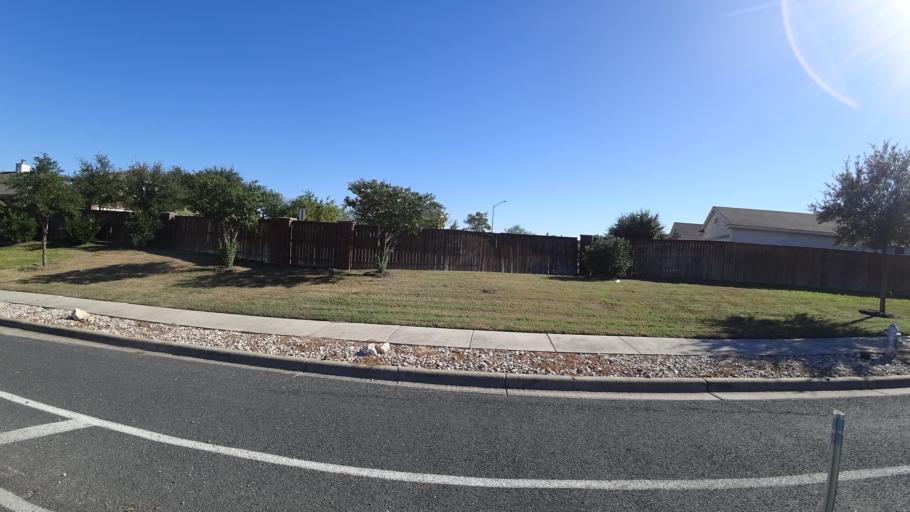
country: US
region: Texas
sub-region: Travis County
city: Austin
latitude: 30.2927
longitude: -97.6676
